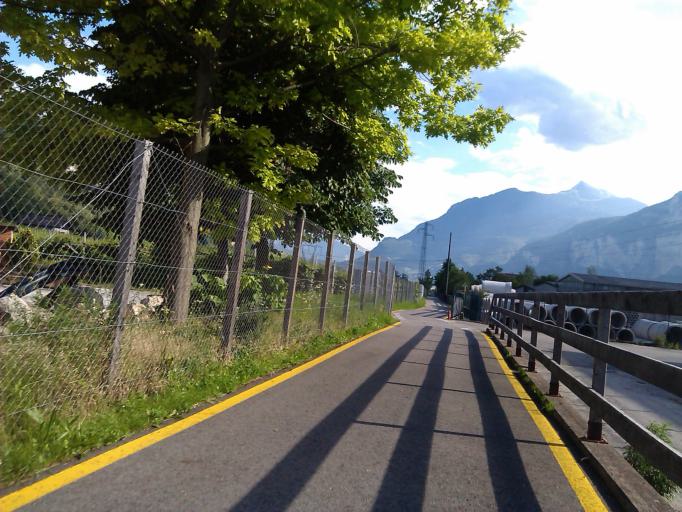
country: IT
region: Trentino-Alto Adige
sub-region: Provincia di Trento
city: Meano
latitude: 46.1235
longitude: 11.1091
